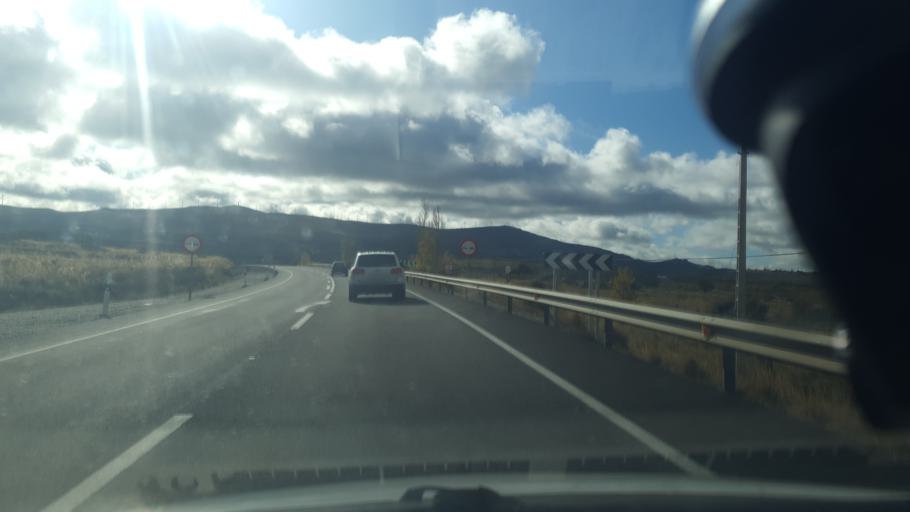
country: ES
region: Castille and Leon
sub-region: Provincia de Segovia
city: Villacastin
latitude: 40.7647
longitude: -4.4340
